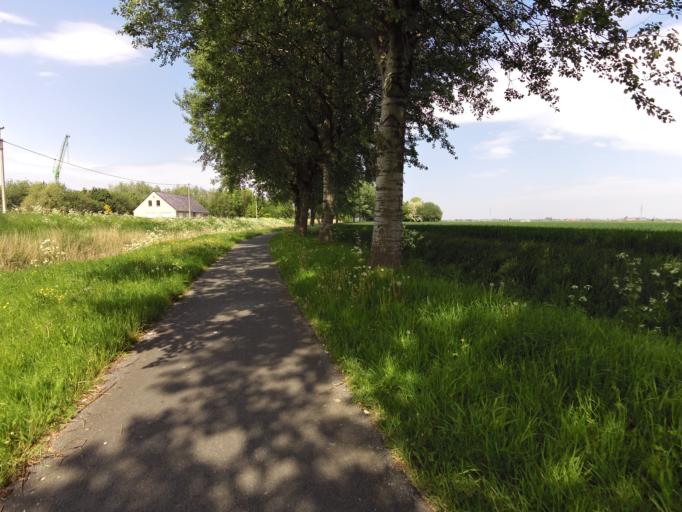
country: BE
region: Flanders
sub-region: Provincie West-Vlaanderen
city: Bredene
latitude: 51.2164
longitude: 2.9976
